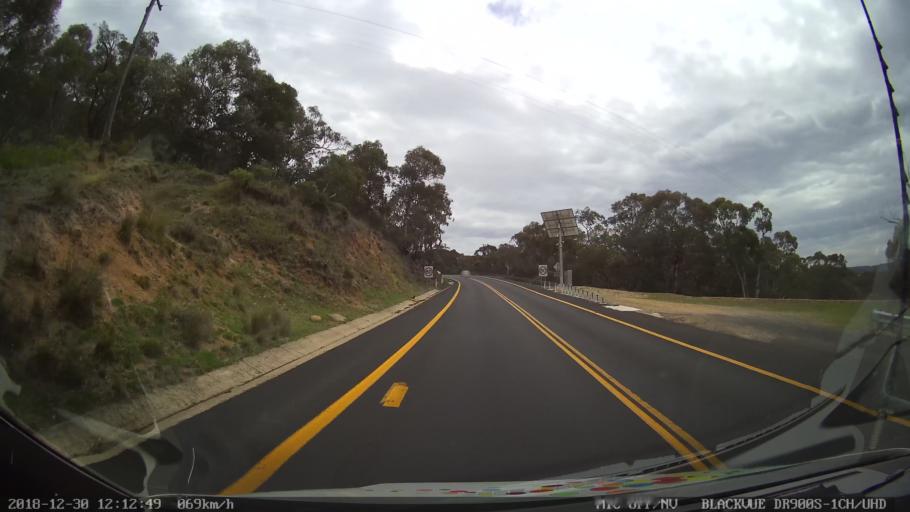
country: AU
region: New South Wales
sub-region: Snowy River
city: Jindabyne
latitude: -36.3542
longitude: 148.5866
